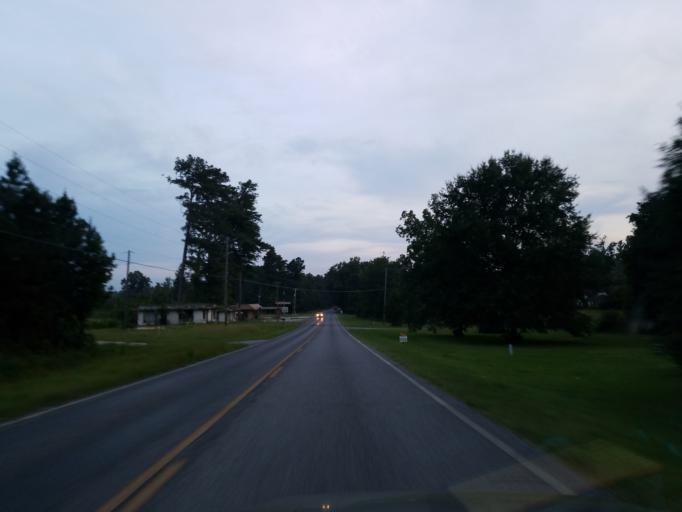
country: US
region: Mississippi
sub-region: Jones County
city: Sharon
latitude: 31.9066
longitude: -88.9325
